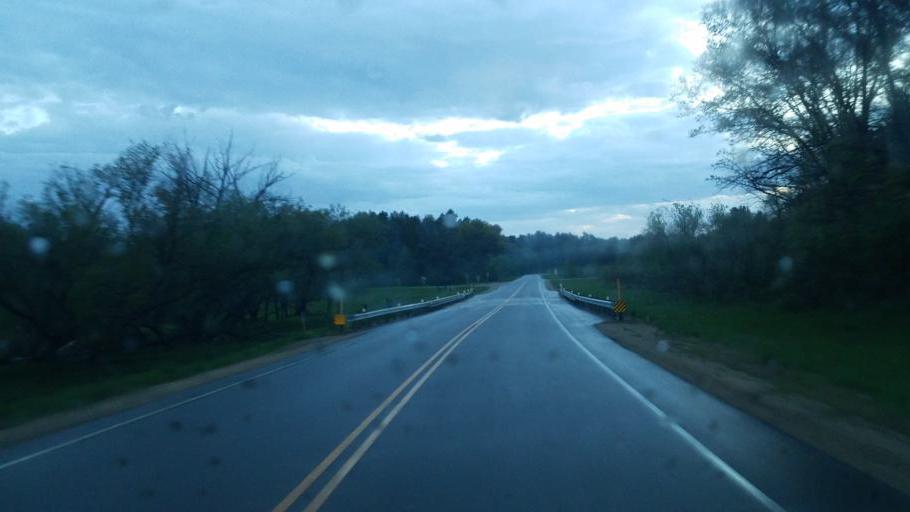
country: US
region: Wisconsin
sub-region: Juneau County
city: Elroy
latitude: 43.7841
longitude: -90.2761
